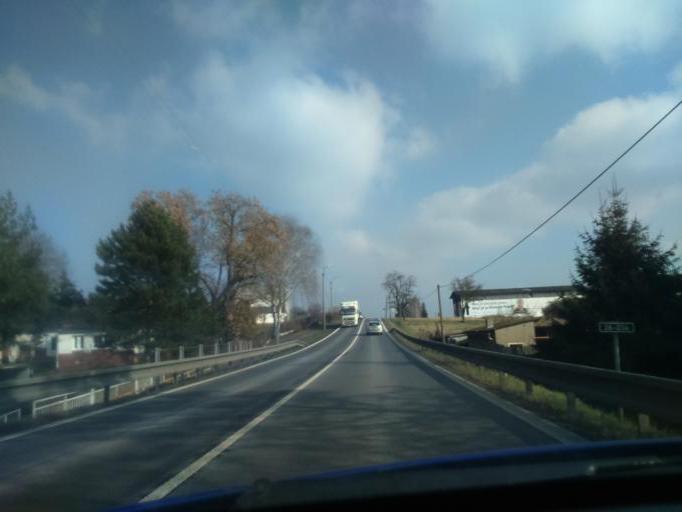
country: CZ
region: Plzensky
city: Blizejov
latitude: 49.5384
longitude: 12.9860
